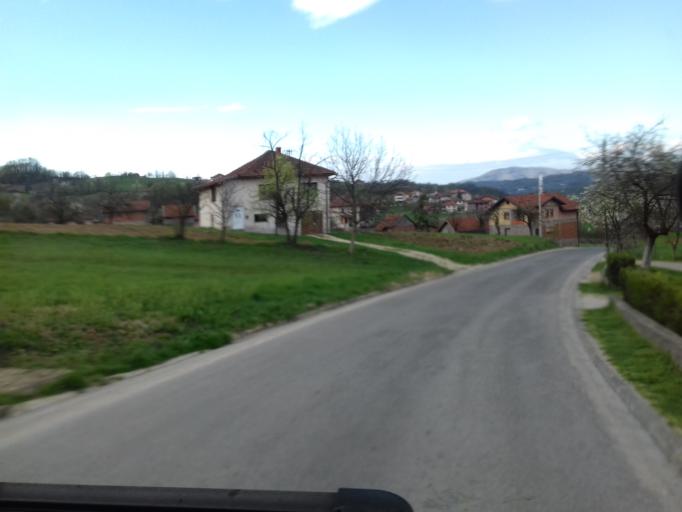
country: BA
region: Federation of Bosnia and Herzegovina
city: Tesanjka
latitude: 44.6468
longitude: 18.0282
